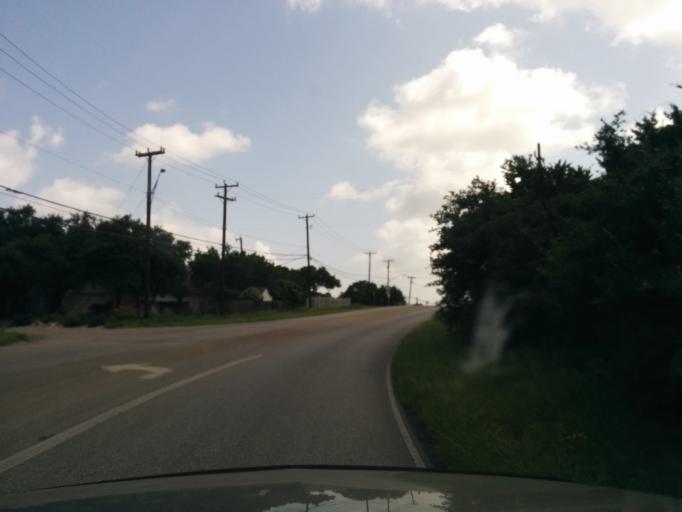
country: US
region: Texas
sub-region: Bexar County
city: Cross Mountain
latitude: 29.5964
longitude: -98.6307
